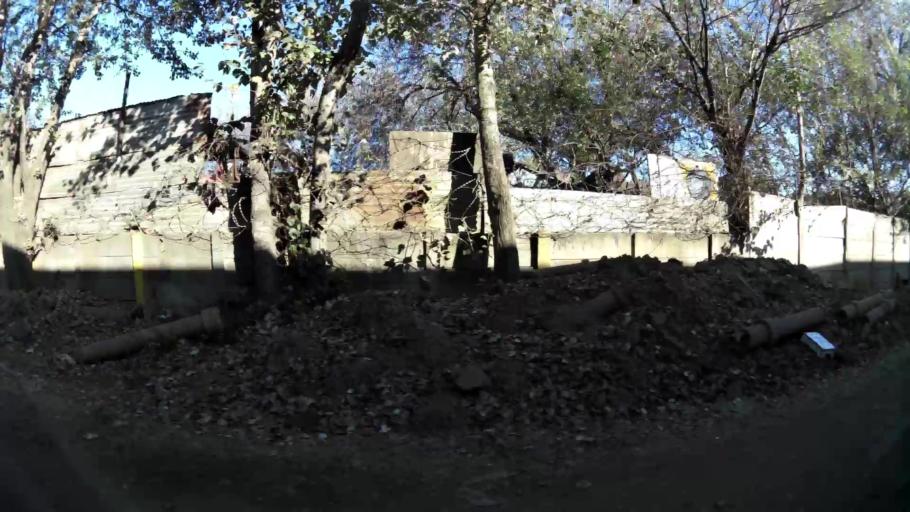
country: ZA
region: Gauteng
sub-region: City of Johannesburg Metropolitan Municipality
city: Johannesburg
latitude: -26.2088
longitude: 27.9917
